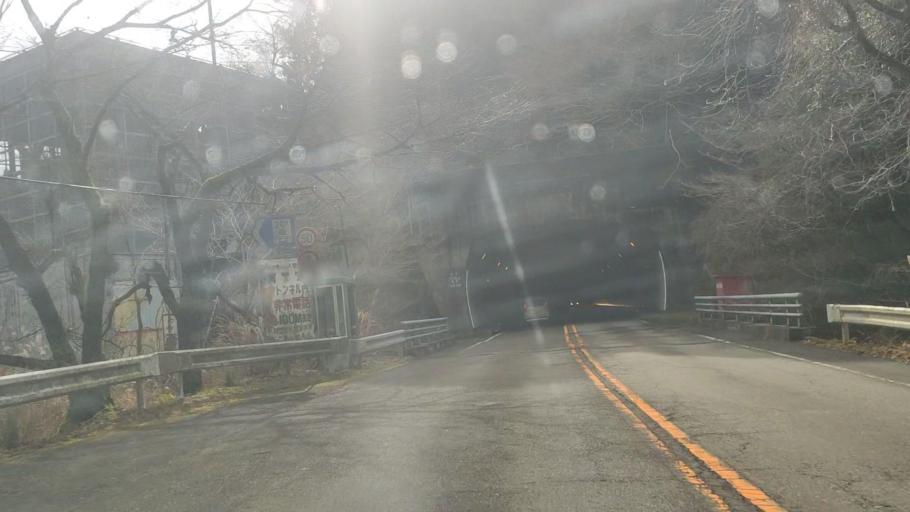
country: JP
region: Kumamoto
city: Hitoyoshi
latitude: 32.1050
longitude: 130.8052
